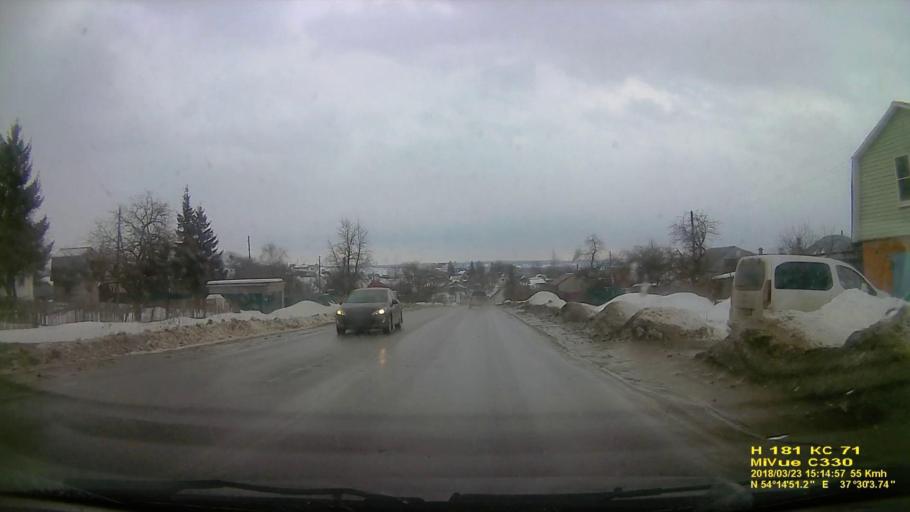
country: RU
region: Tula
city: Barsuki
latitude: 54.2475
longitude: 37.5010
